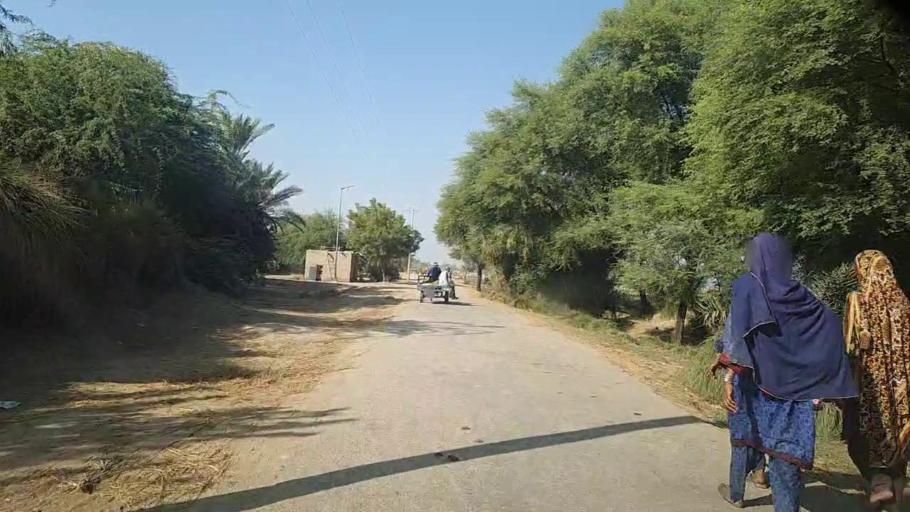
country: PK
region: Sindh
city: Tangwani
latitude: 28.2467
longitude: 68.9962
